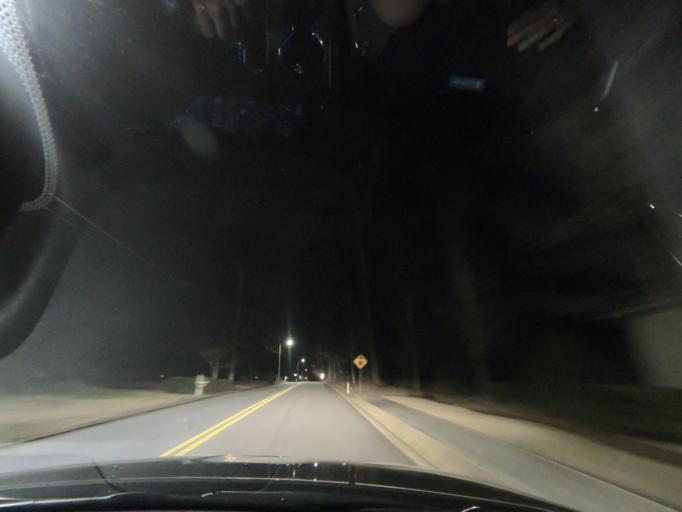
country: US
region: Georgia
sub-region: Fulton County
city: College Park
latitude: 33.6604
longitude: -84.4695
